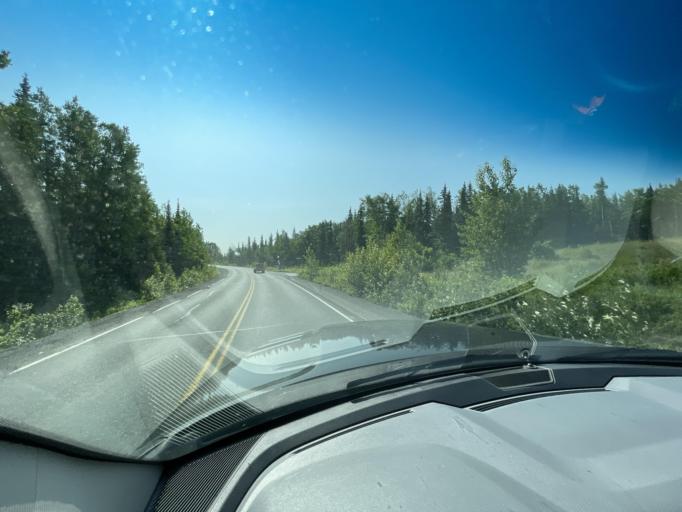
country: US
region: Alaska
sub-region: Kenai Peninsula Borough
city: Cohoe
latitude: 60.3005
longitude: -151.2831
